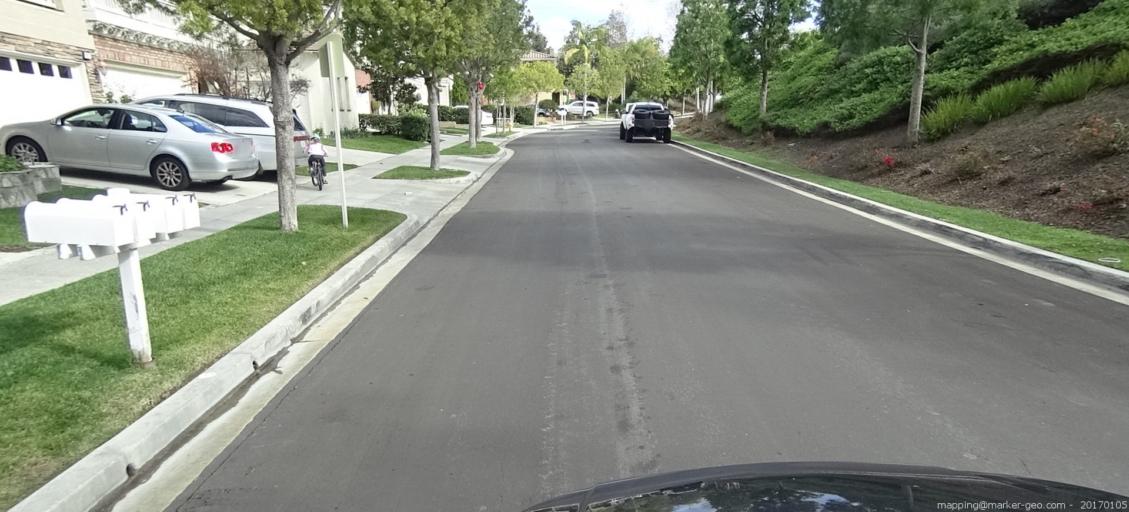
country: US
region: California
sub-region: Orange County
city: Ladera Ranch
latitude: 33.5651
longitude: -117.6414
